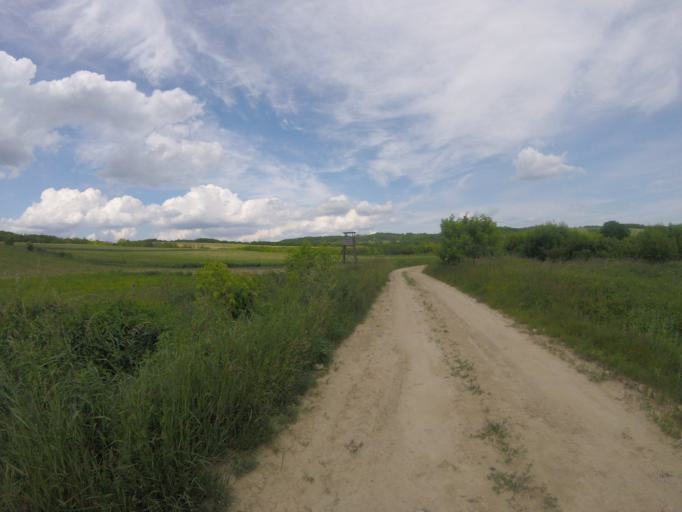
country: HU
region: Zala
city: Zalaszentgrot
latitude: 46.8934
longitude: 17.0521
